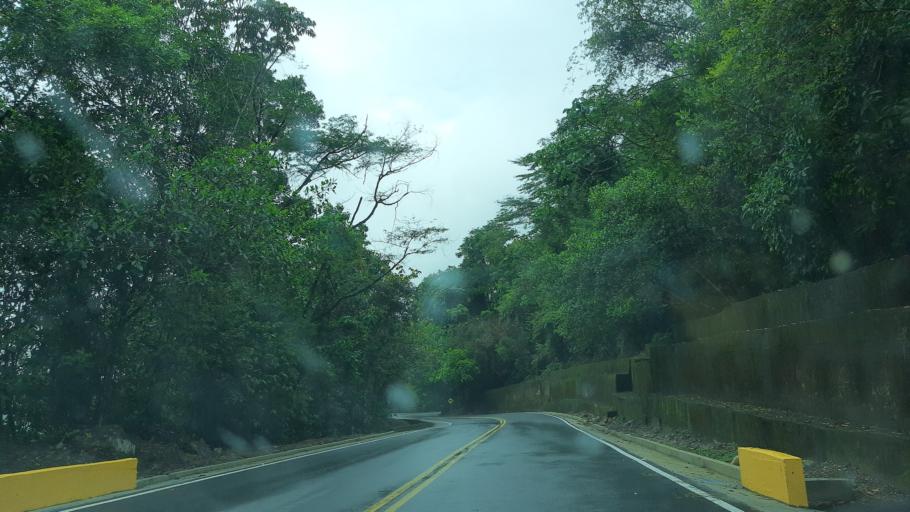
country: CO
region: Casanare
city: Sabanalarga
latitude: 4.7592
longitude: -73.0275
